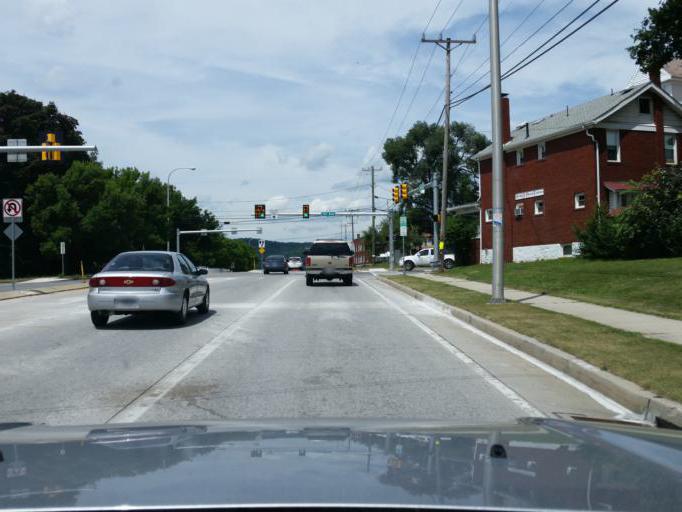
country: US
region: Pennsylvania
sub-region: Blair County
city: Altoona
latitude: 40.5044
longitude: -78.3959
